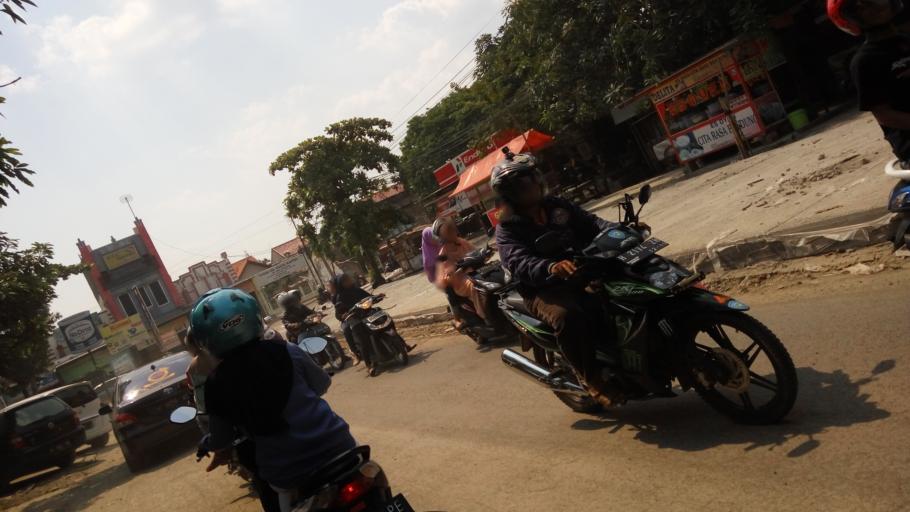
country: ID
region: Central Java
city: Mranggen
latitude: -7.0373
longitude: 110.4723
